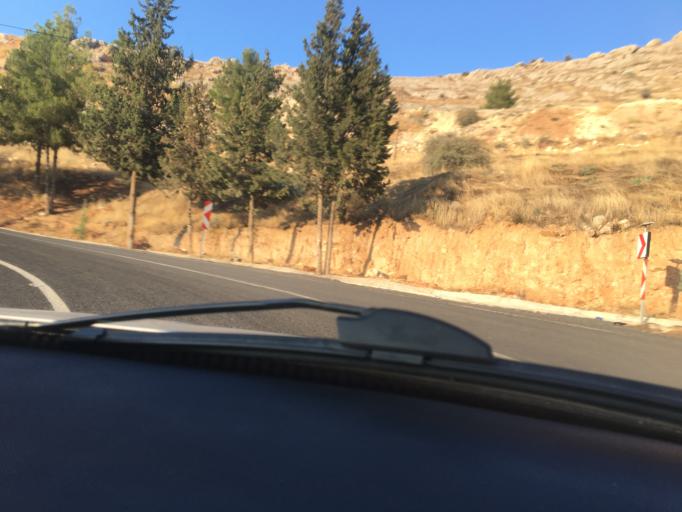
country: TR
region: Sanliurfa
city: Halfeti
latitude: 37.2438
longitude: 37.8741
